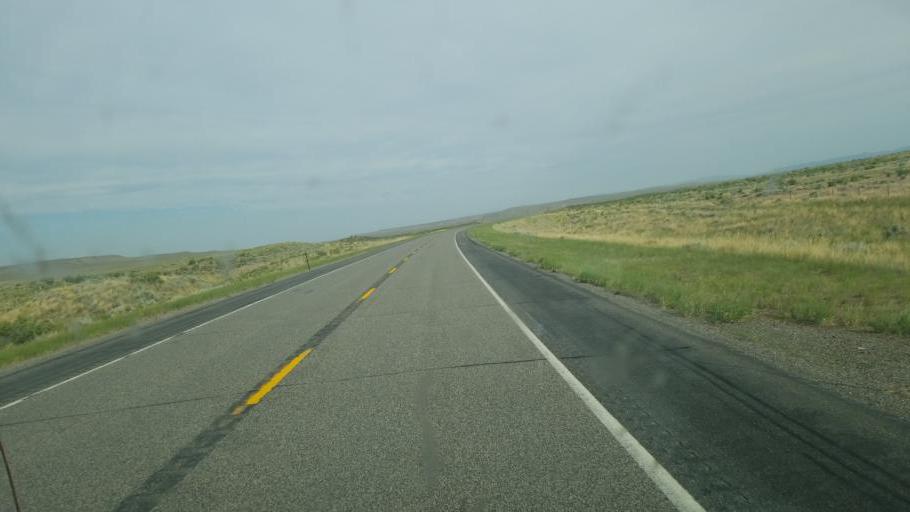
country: US
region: Wyoming
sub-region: Fremont County
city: Riverton
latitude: 43.1906
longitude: -107.9045
